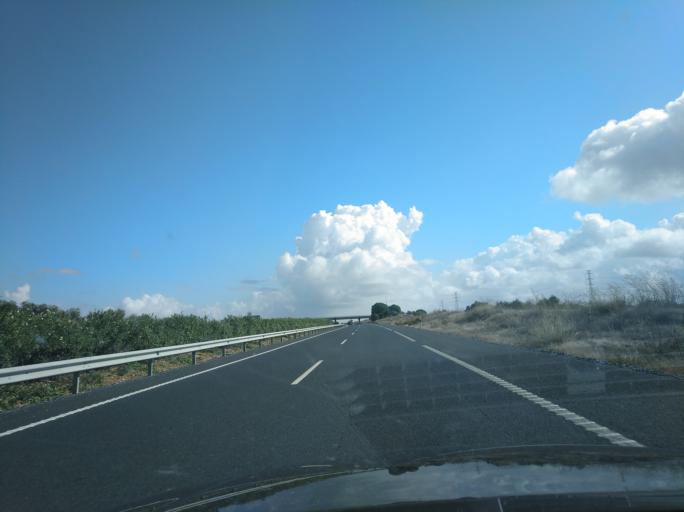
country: ES
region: Andalusia
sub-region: Provincia de Huelva
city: Chucena
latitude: 37.3536
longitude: -6.3760
